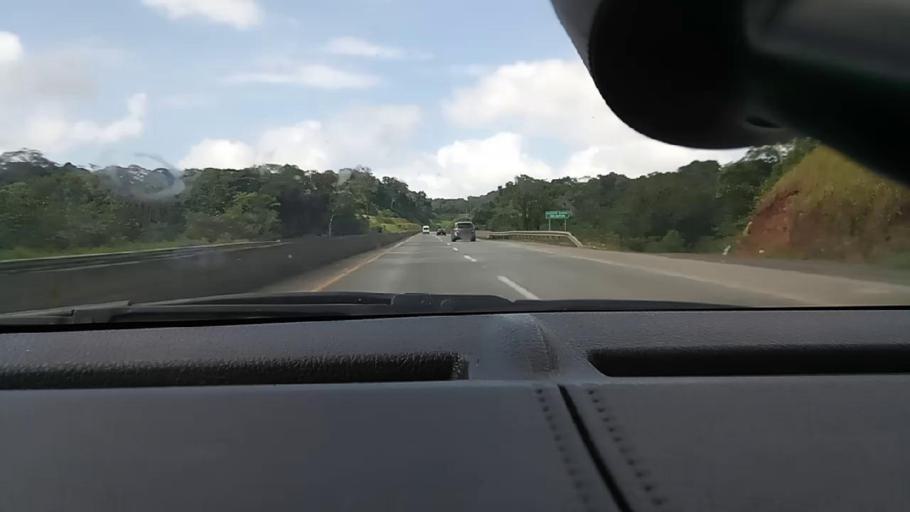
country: PA
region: Colon
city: Gatun
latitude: 9.2823
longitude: -79.7696
